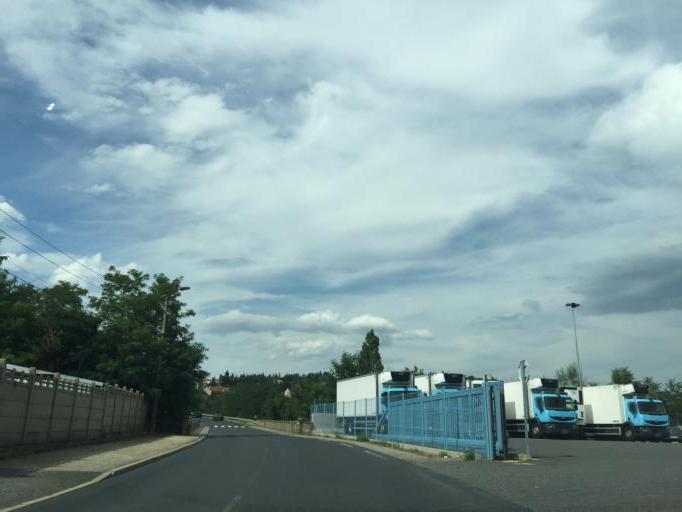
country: FR
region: Rhone-Alpes
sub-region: Departement de la Loire
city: Saint-Jean-Bonnefonds
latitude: 45.4409
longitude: 4.4293
